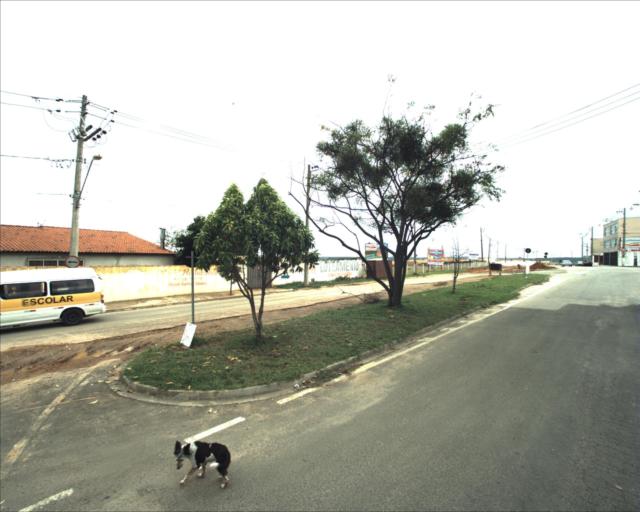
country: BR
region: Sao Paulo
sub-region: Sorocaba
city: Sorocaba
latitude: -23.4262
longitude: -47.4676
